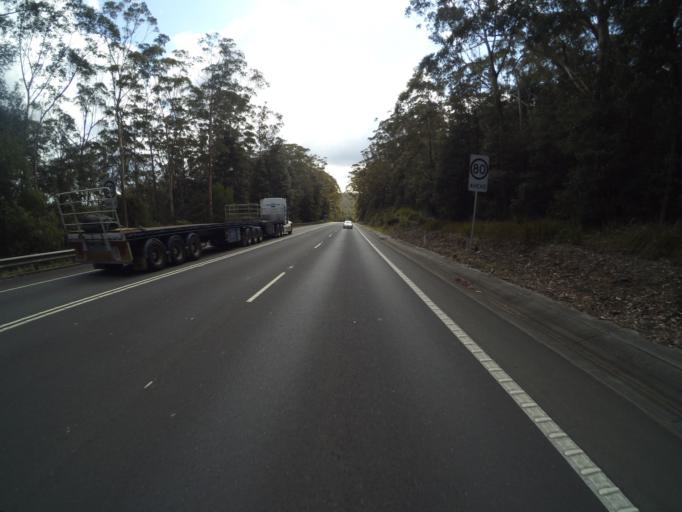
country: AU
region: New South Wales
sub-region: Wollongong
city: Mount Ousley
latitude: -34.3686
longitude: 150.8493
